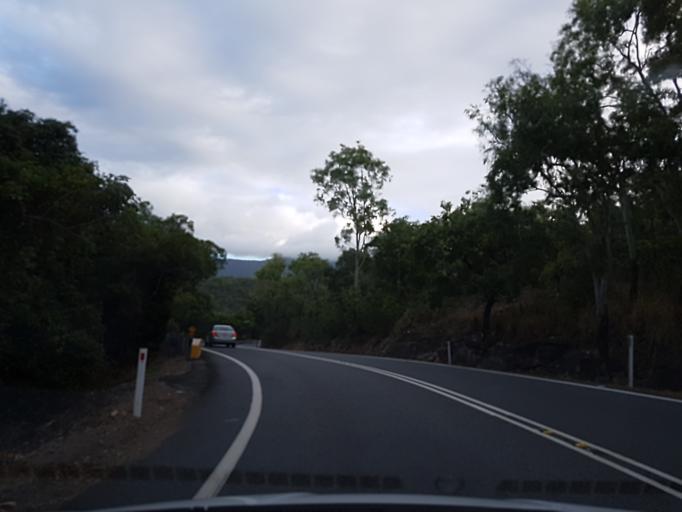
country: AU
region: Queensland
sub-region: Cairns
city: Palm Cove
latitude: -16.6511
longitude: 145.5649
